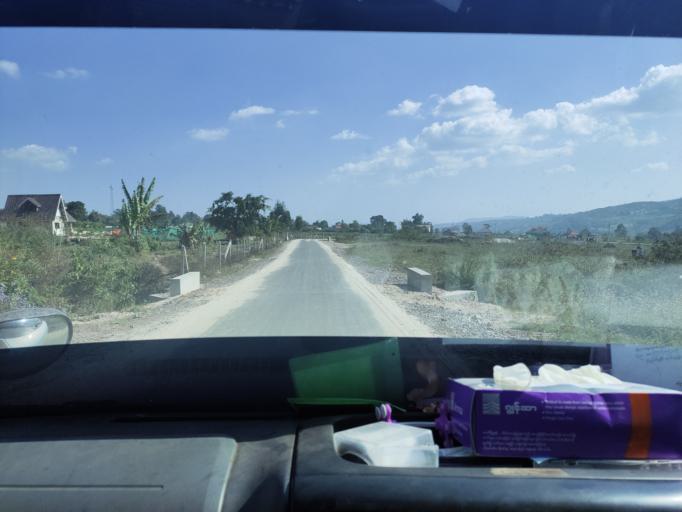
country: MM
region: Mandalay
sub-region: Pyin Oo Lwin District
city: Pyin Oo Lwin
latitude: 22.0670
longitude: 96.5324
